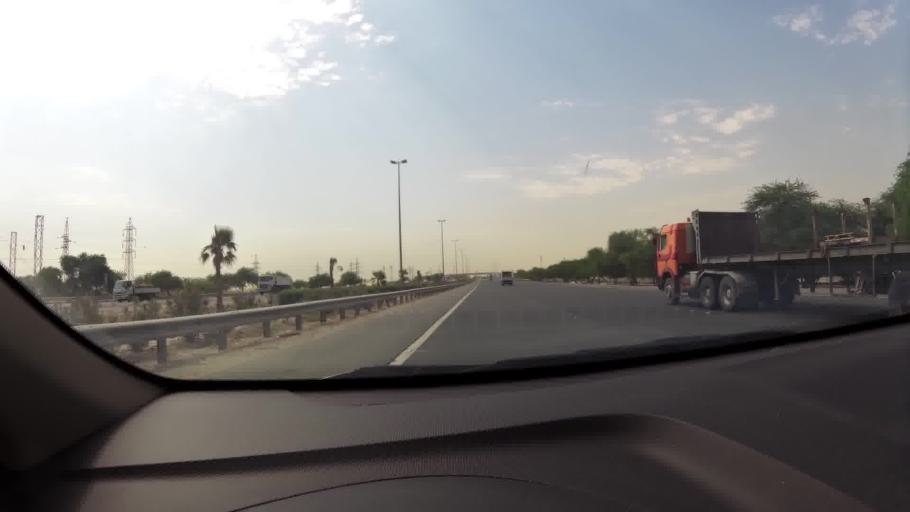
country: KW
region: Al Ahmadi
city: Al Fahahil
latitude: 28.8700
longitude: 48.2344
